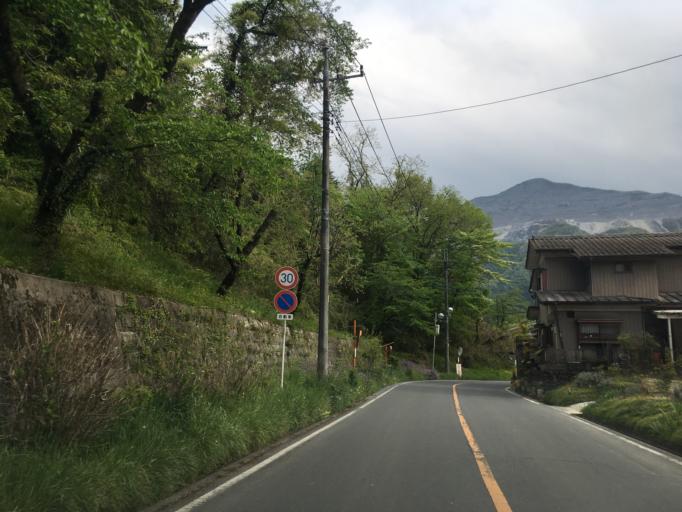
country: JP
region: Saitama
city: Chichibu
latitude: 35.9816
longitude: 139.1015
